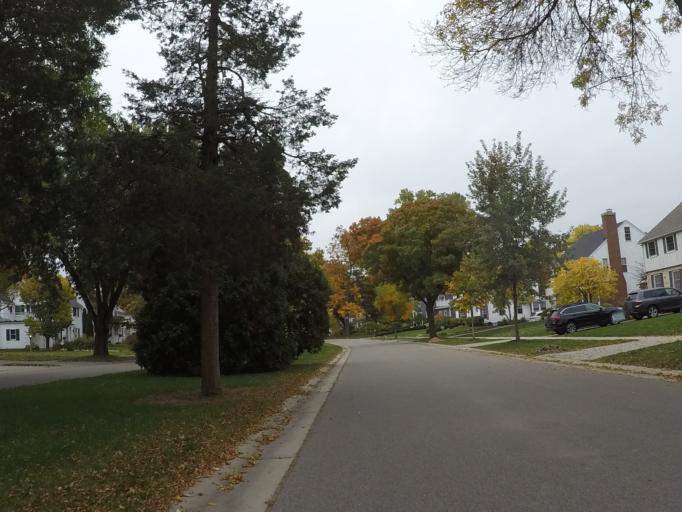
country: US
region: Wisconsin
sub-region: Dane County
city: Maple Bluff
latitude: 43.1068
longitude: -89.3670
